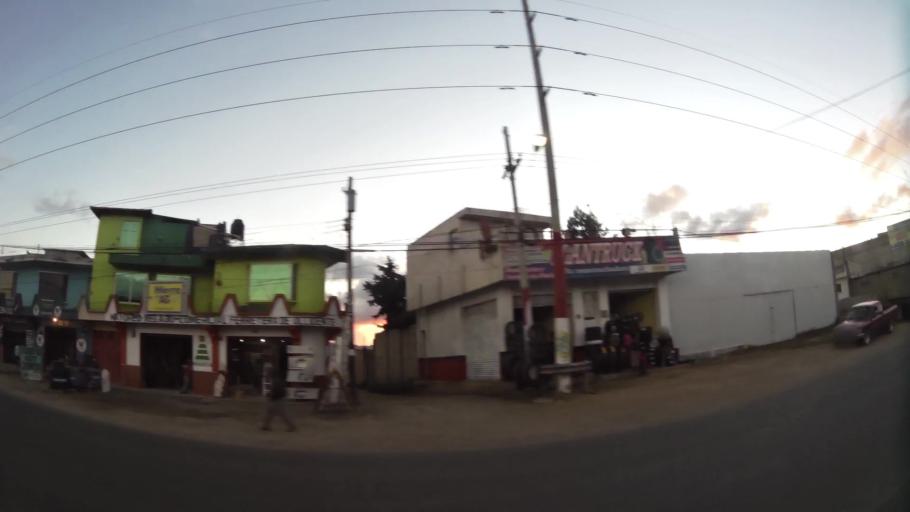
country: GT
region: Quetzaltenango
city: Olintepeque
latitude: 14.8607
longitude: -91.5242
